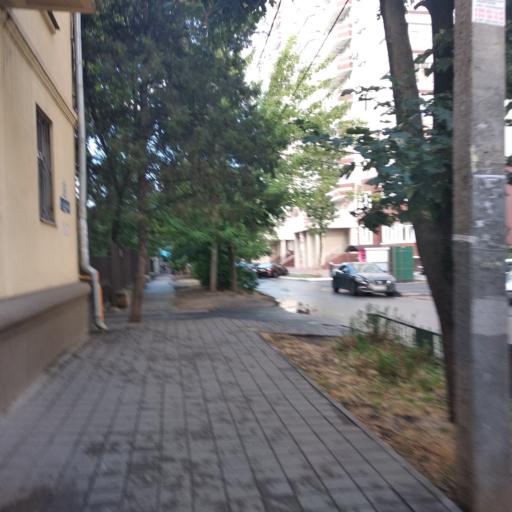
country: RU
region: Krasnodarskiy
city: Krasnodar
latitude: 45.0176
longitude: 38.9608
